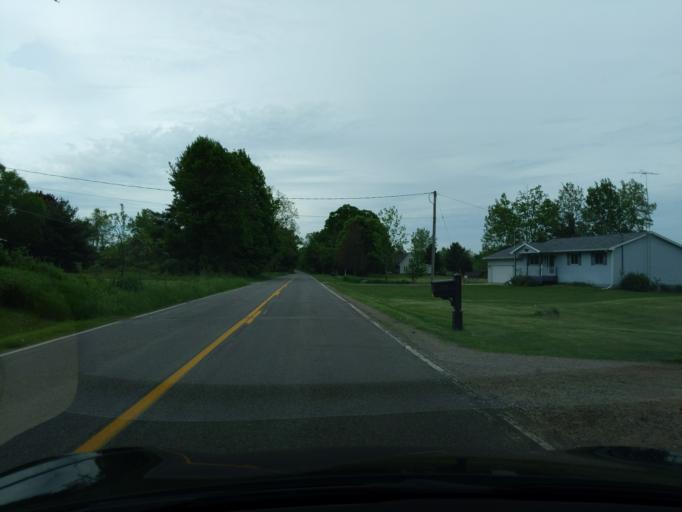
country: US
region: Michigan
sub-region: Ingham County
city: Leslie
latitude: 42.4062
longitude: -84.3541
